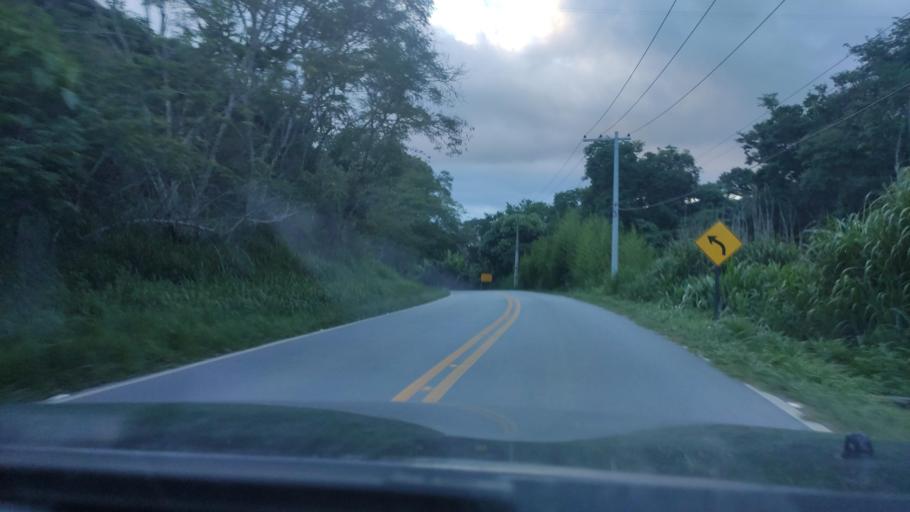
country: BR
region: Sao Paulo
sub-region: Campos Do Jordao
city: Campos do Jordao
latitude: -22.8248
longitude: -45.6767
